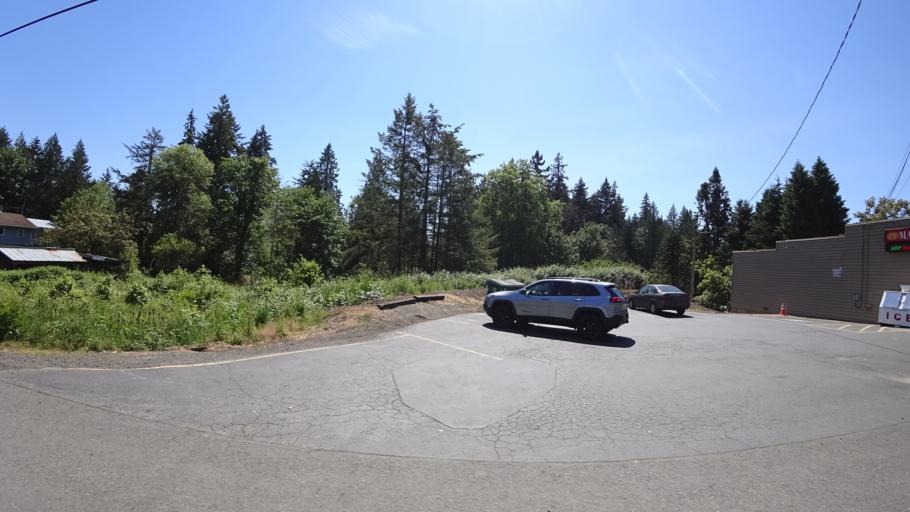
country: US
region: Oregon
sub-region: Clackamas County
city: Happy Valley
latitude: 45.4690
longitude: -122.4889
